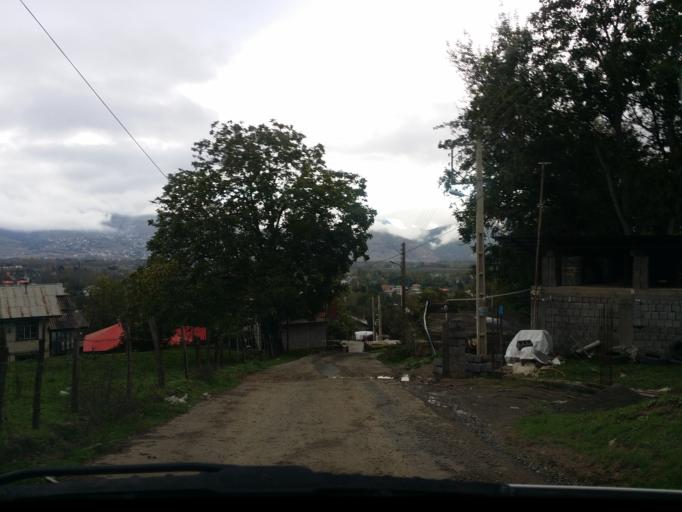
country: IR
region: Mazandaran
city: `Abbasabad
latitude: 36.5027
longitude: 51.1899
